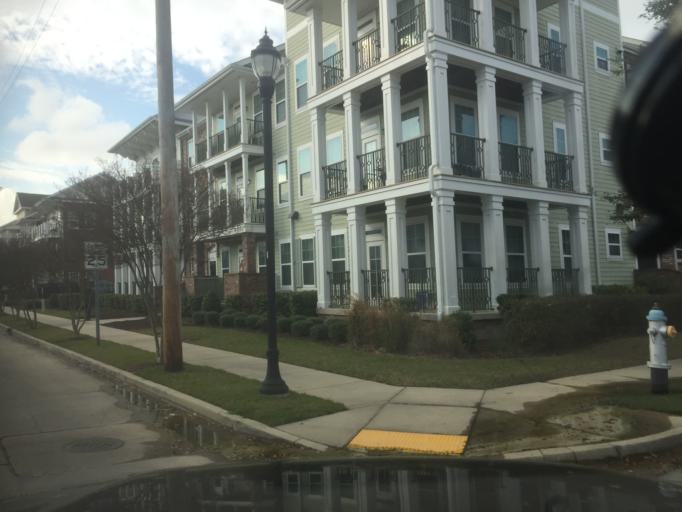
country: US
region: Louisiana
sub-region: Orleans Parish
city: New Orleans
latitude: 29.9980
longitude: -90.0750
